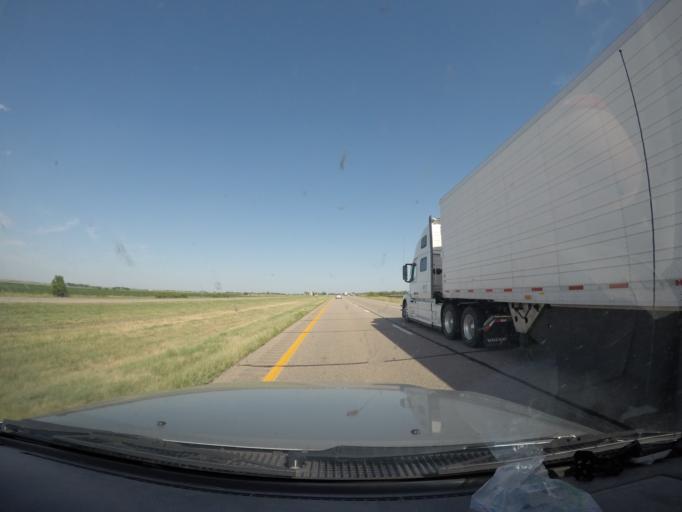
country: US
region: Nebraska
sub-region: Phelps County
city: Holdrege
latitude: 40.6898
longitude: -99.3377
